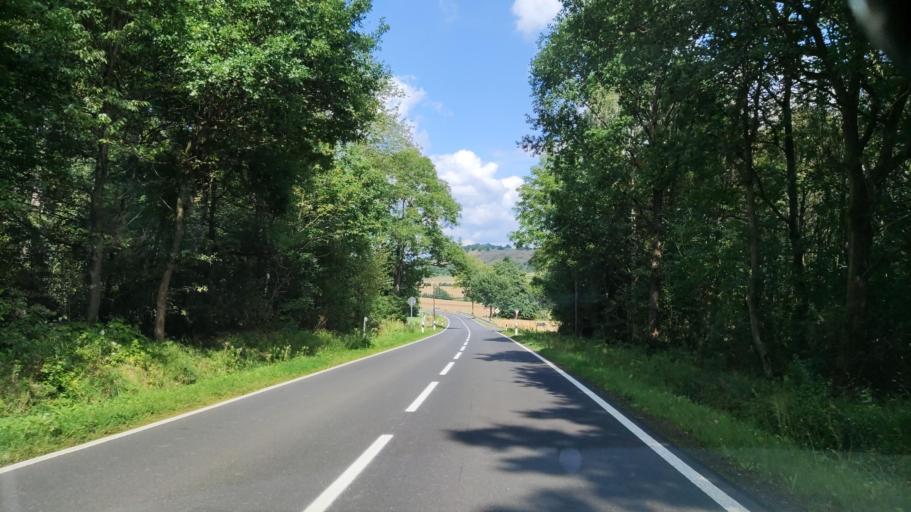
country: DE
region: Lower Saxony
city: Hardegsen
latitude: 51.7207
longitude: 9.7851
